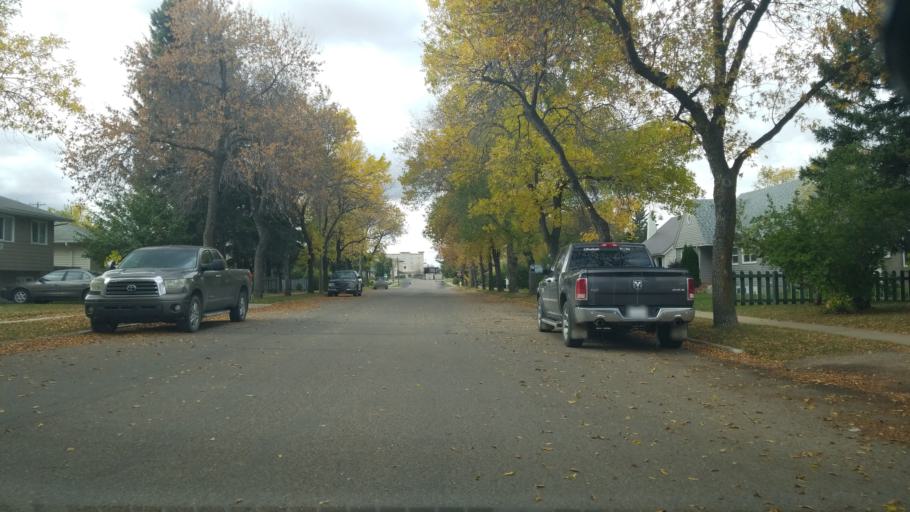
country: CA
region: Saskatchewan
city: Lloydminster
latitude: 53.2790
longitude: -110.0159
